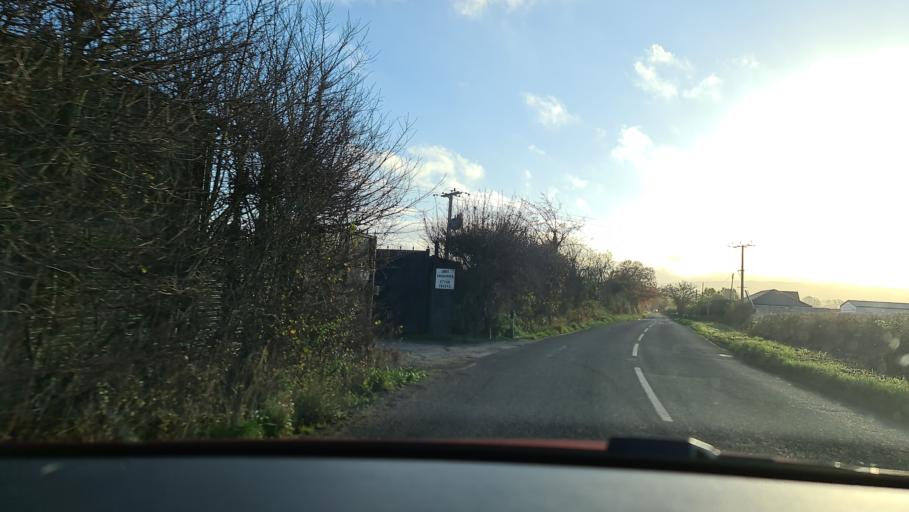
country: GB
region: England
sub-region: Buckinghamshire
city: Aylesbury
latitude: 51.7804
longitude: -0.8132
